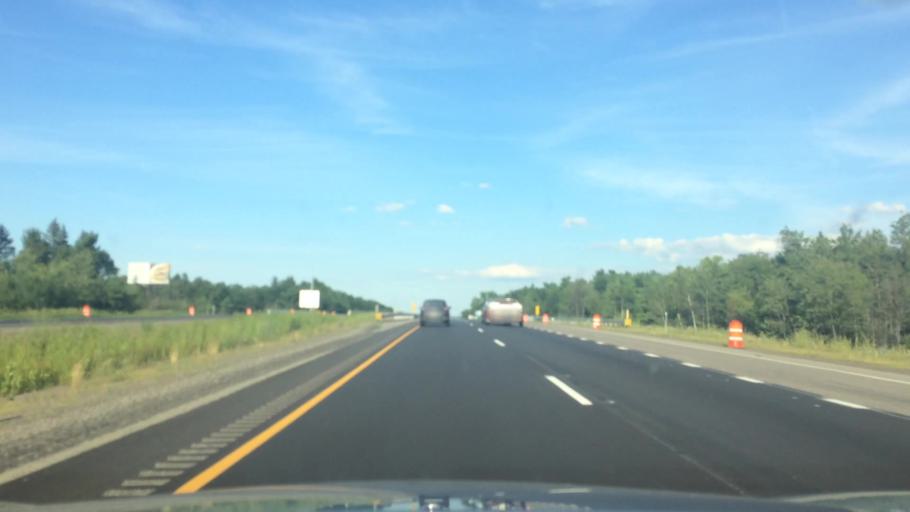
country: US
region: Wisconsin
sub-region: Portage County
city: Stevens Point
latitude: 44.5482
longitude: -89.5720
